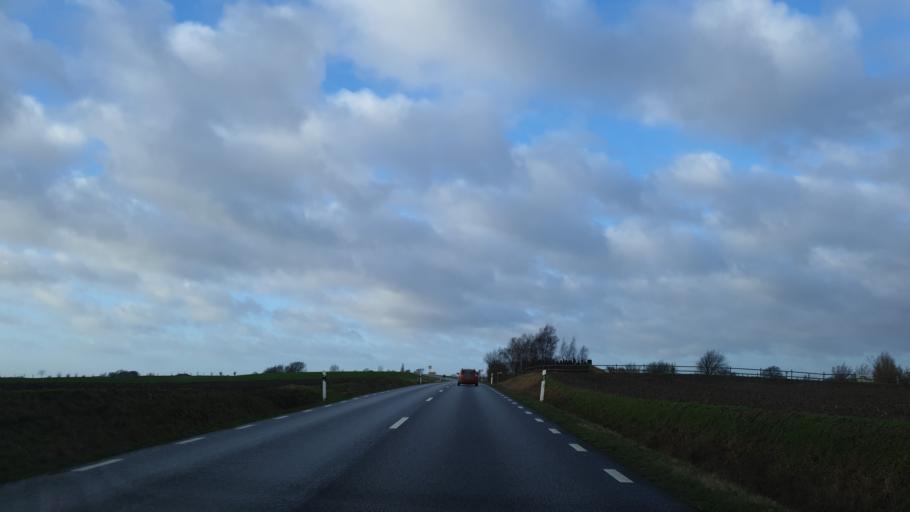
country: SE
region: Skane
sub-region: Trelleborgs Kommun
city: Trelleborg
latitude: 55.4573
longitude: 13.1669
